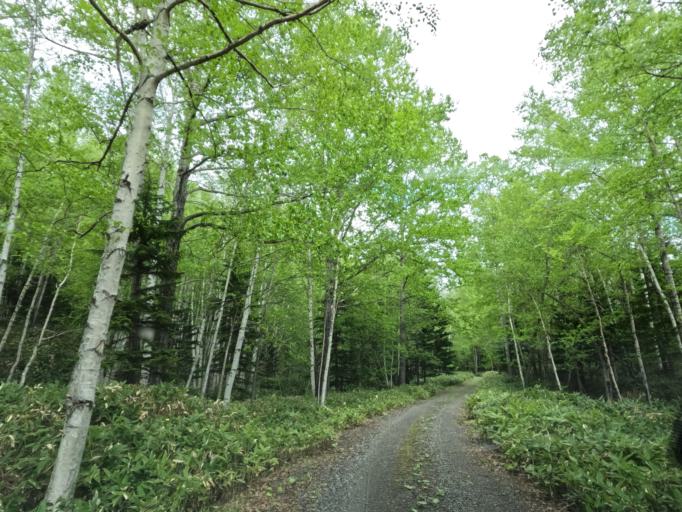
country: JP
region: Hokkaido
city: Kamikawa
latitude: 43.6452
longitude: 143.0219
